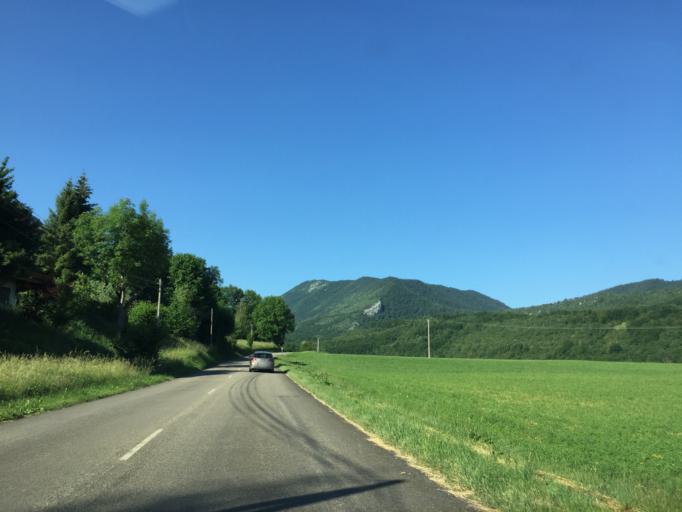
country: FR
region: Rhone-Alpes
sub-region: Departement de la Drome
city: Saint-Laurent-en-Royans
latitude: 44.9596
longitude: 5.4087
